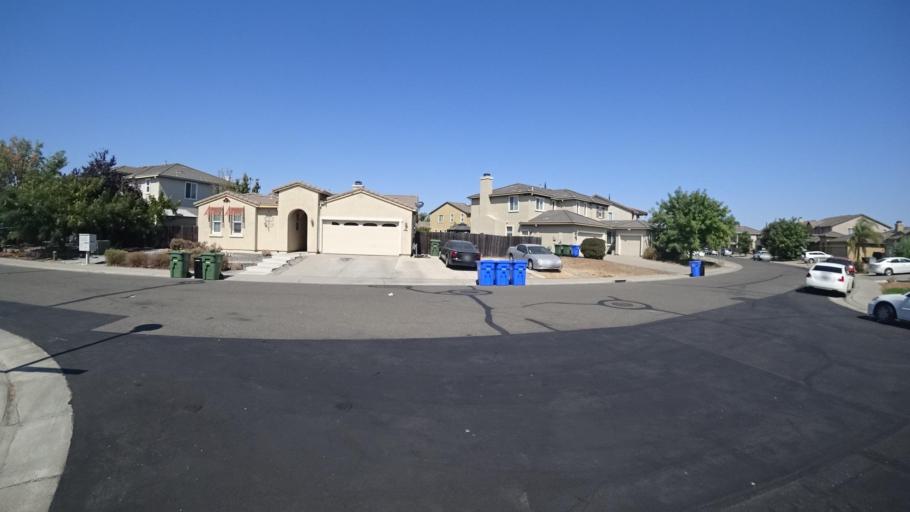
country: US
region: California
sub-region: Sacramento County
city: Laguna
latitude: 38.4420
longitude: -121.3954
